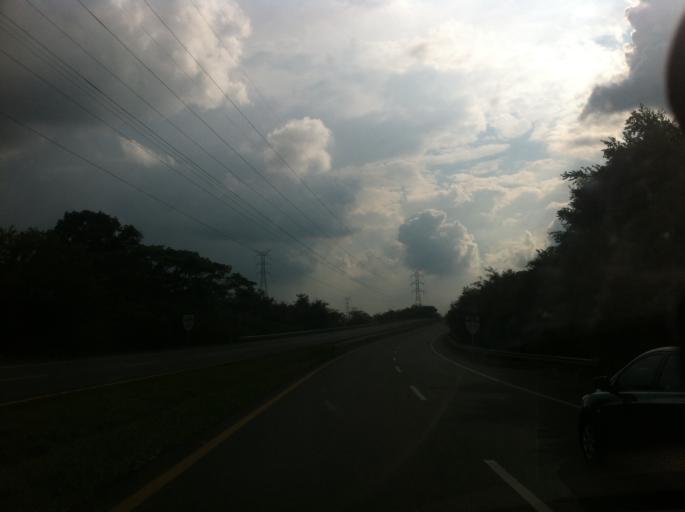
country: CO
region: Valle del Cauca
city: Tulua
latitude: 4.0696
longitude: -76.1786
